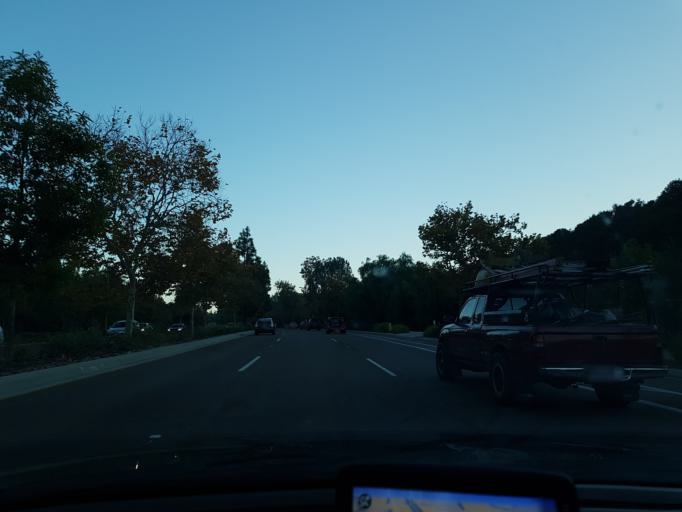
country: US
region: California
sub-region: San Diego County
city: Fairbanks Ranch
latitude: 32.9319
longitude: -117.1260
